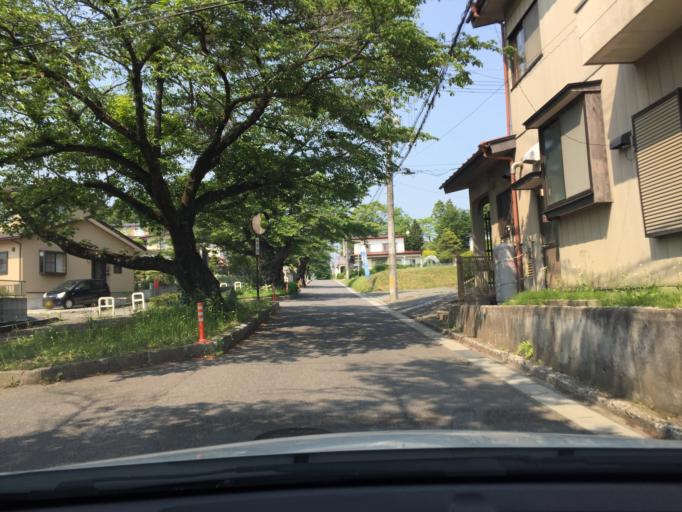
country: JP
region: Tochigi
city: Kuroiso
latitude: 37.1174
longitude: 140.2100
